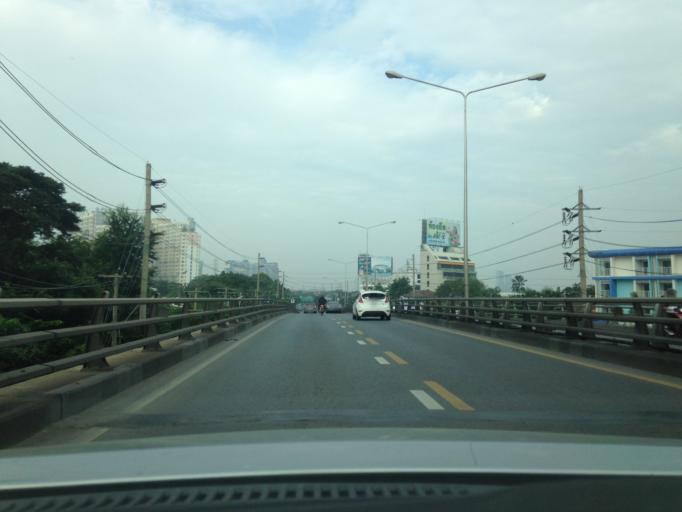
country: TH
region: Bangkok
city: Bang Sue
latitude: 13.8304
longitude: 100.5388
